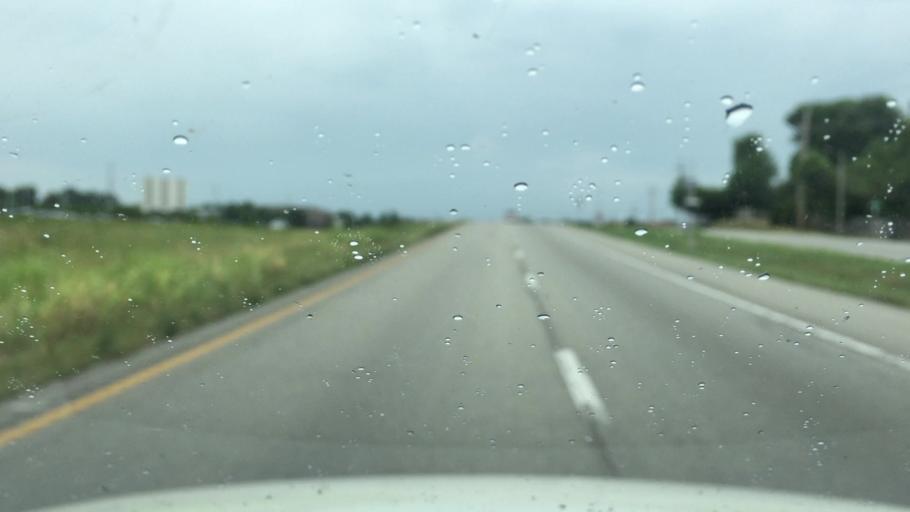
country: US
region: Missouri
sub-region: Jackson County
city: Lees Summit
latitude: 38.9025
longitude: -94.3468
